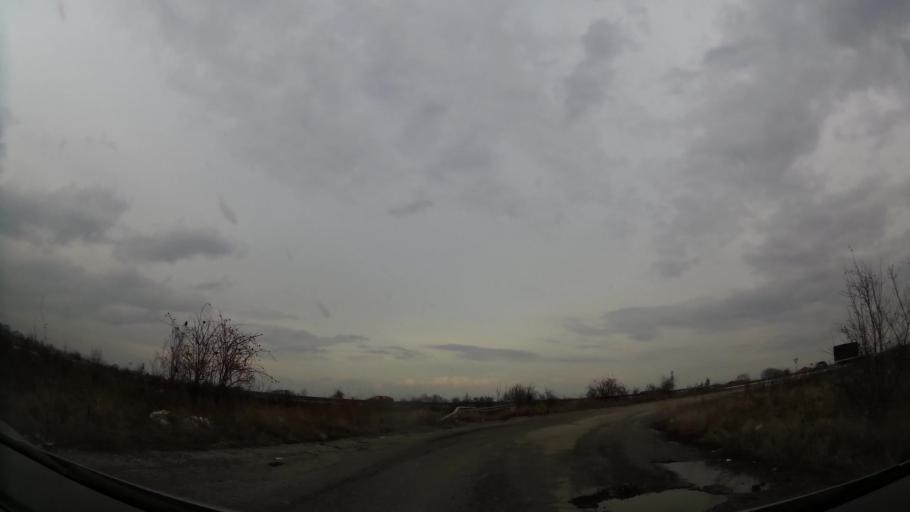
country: BG
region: Sofiya
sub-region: Obshtina Bozhurishte
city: Bozhurishte
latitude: 42.7139
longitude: 23.2184
